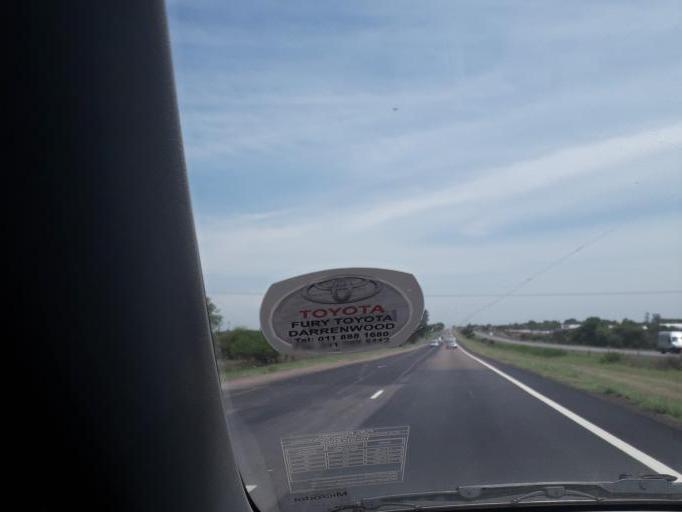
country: ZA
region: Gauteng
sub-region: City of Tshwane Metropolitan Municipality
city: Pretoria
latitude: -25.5863
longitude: 28.2811
